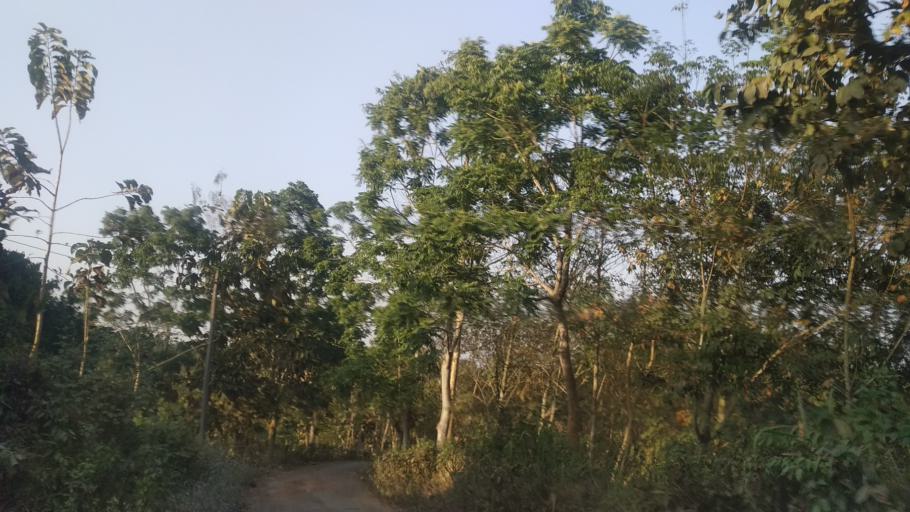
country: IN
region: Tripura
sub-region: West Tripura
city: Sonamura
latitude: 23.4386
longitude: 91.3613
